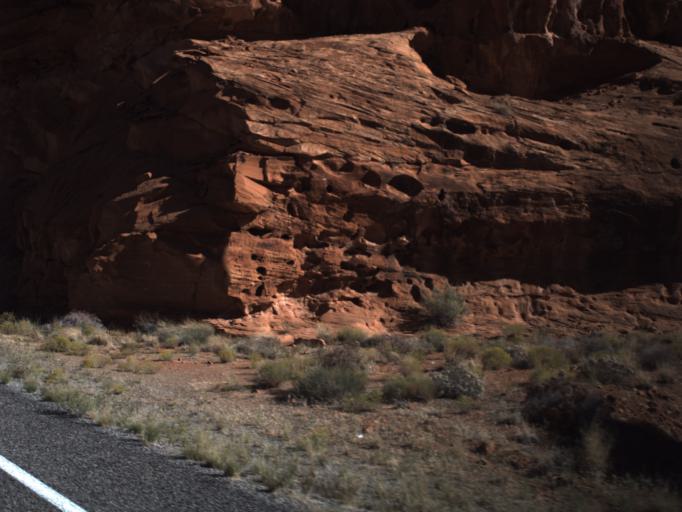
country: US
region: Utah
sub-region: San Juan County
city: Blanding
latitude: 37.9732
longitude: -110.4913
